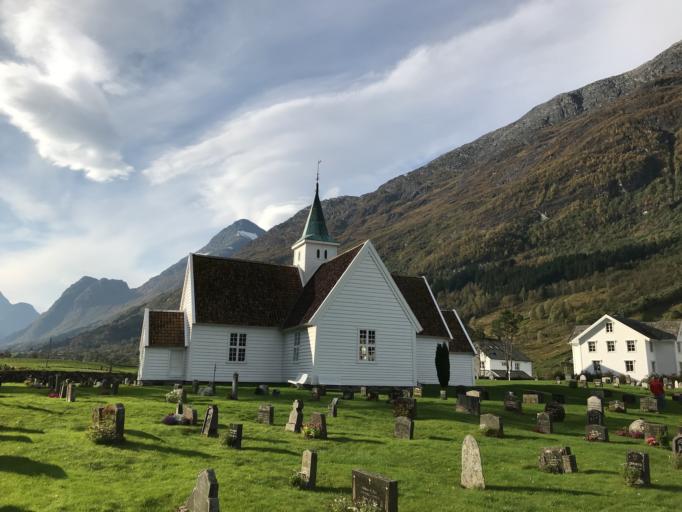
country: NO
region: Sogn og Fjordane
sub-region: Stryn
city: Stryn
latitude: 61.8346
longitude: 6.8060
